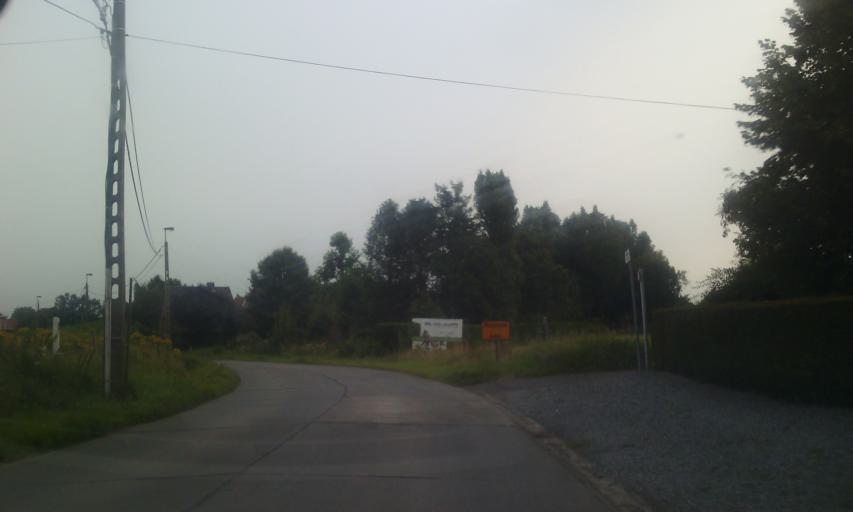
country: BE
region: Flanders
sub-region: Provincie Oost-Vlaanderen
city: Aalst
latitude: 50.9800
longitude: 4.0367
